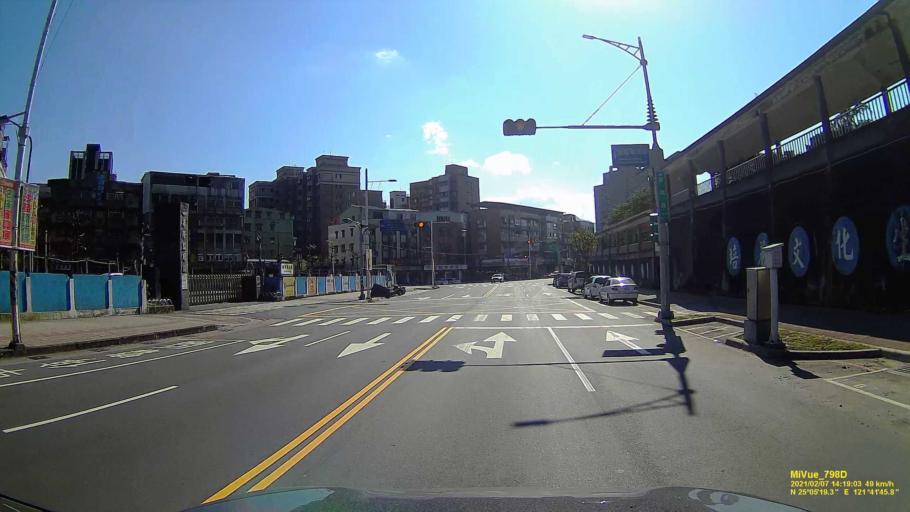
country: TW
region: Taiwan
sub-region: Keelung
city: Keelung
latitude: 25.0885
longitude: 121.6959
